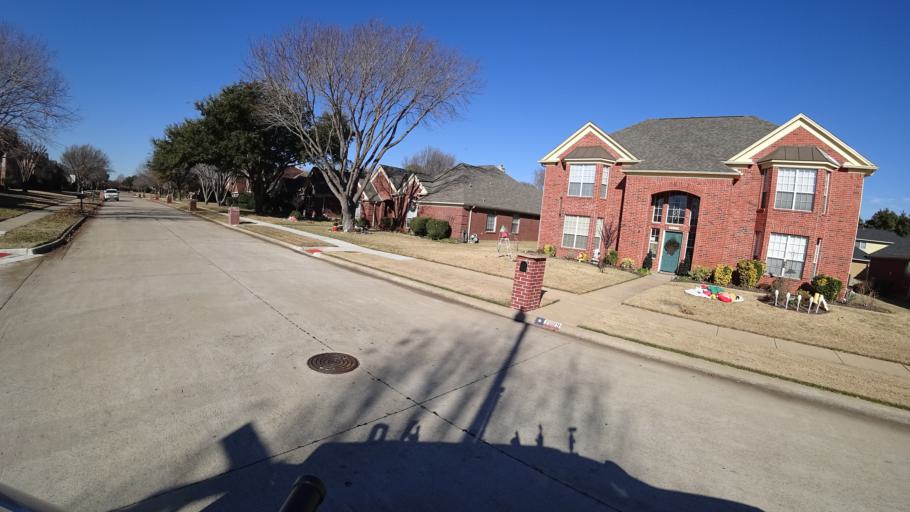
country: US
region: Texas
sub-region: Denton County
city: Lewisville
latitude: 33.0194
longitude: -97.0312
